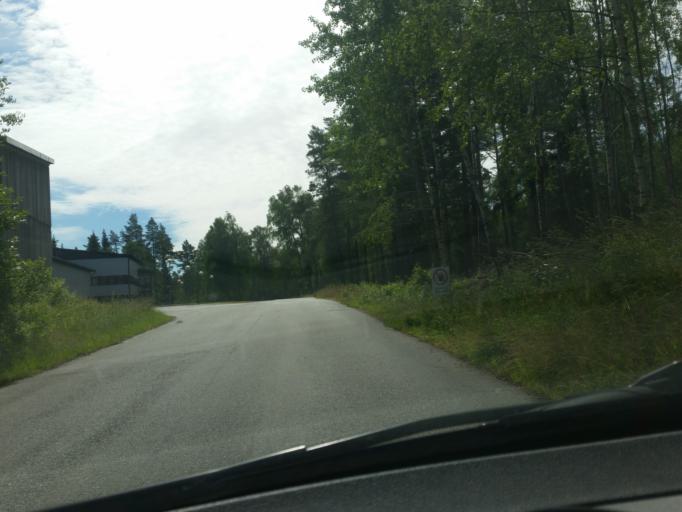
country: SE
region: Vaestra Goetaland
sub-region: Tanums Kommun
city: Tanumshede
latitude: 58.6075
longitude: 11.4720
